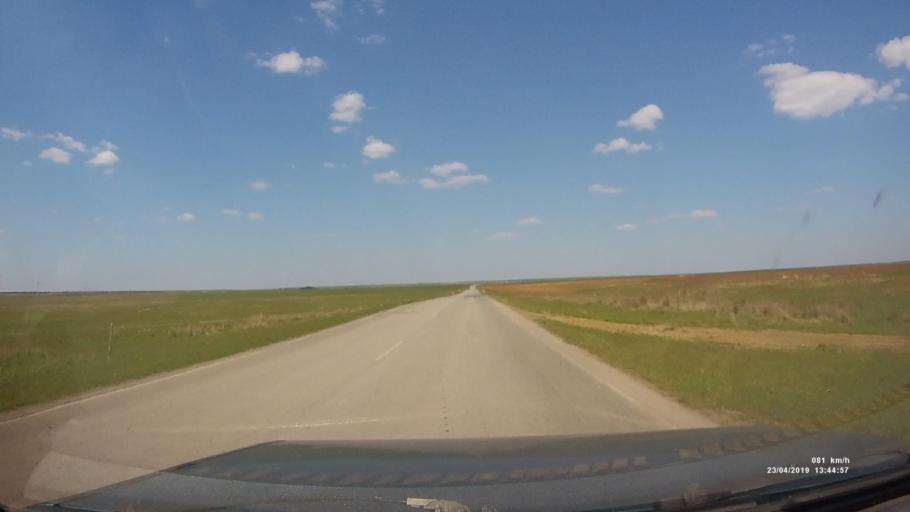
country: RU
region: Kalmykiya
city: Yashalta
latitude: 46.5868
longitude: 42.8192
